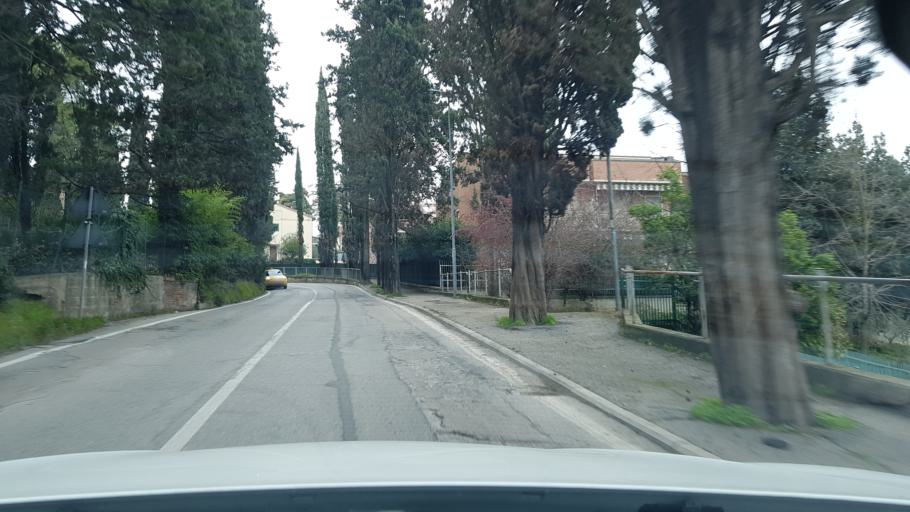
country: IT
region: Umbria
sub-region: Provincia di Perugia
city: Perugia
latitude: 43.1157
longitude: 12.3648
